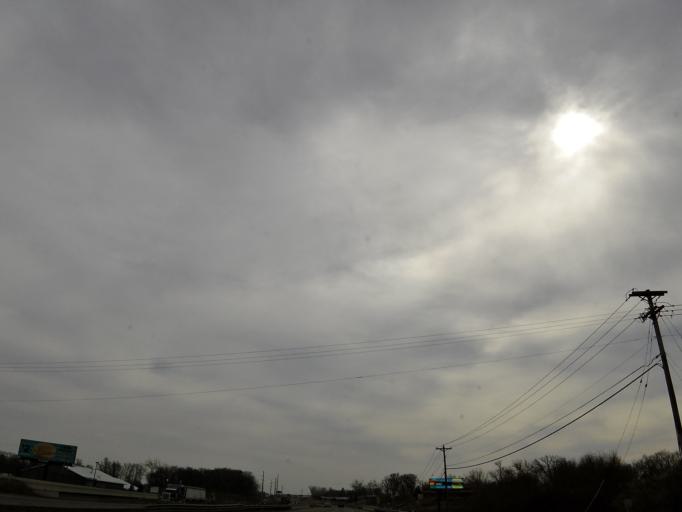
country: US
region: Minnesota
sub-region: Dakota County
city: Inver Grove Heights
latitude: 44.7976
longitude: -93.0384
